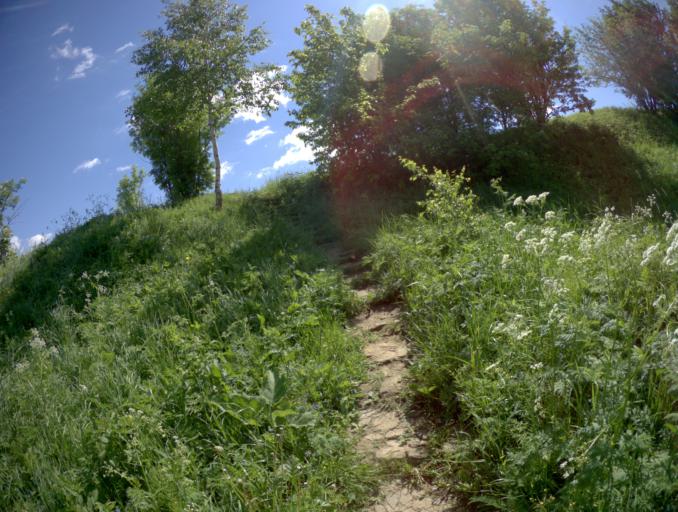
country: RU
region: Ivanovo
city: Gavrilov Posad
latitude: 56.4666
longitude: 40.2259
